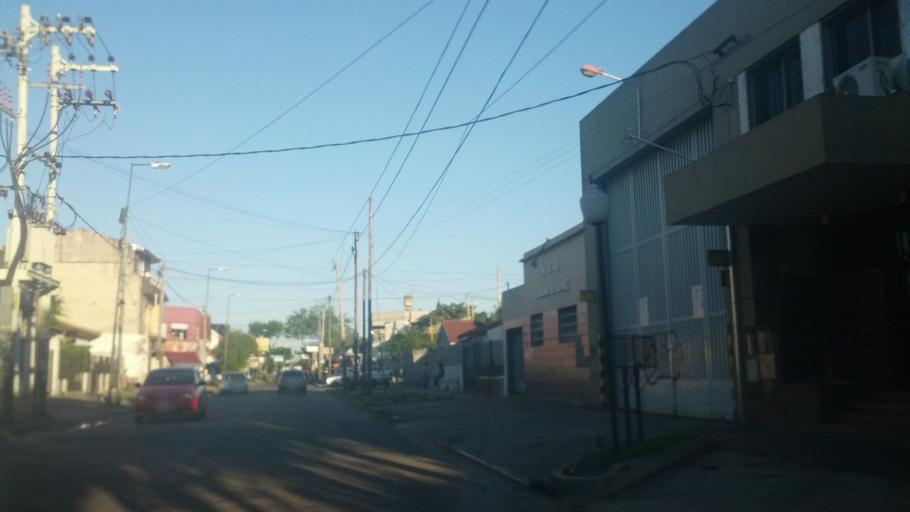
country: AR
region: Buenos Aires
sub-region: Partido de Lomas de Zamora
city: Lomas de Zamora
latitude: -34.7661
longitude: -58.4227
